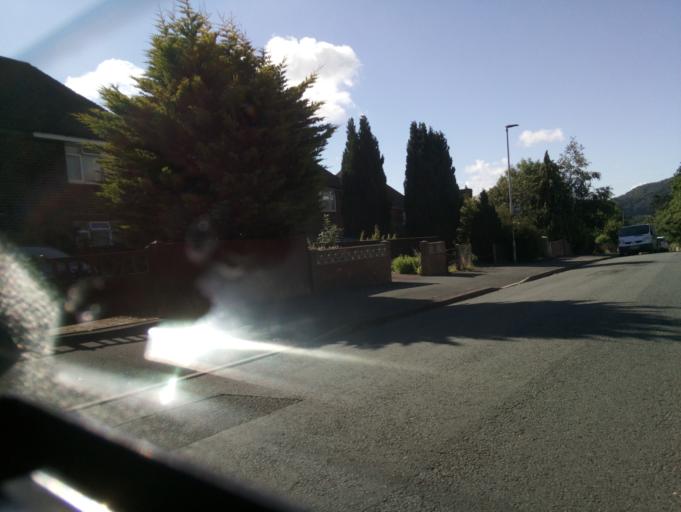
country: GB
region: England
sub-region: Herefordshire
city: Ross on Wye
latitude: 51.9225
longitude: -2.5819
